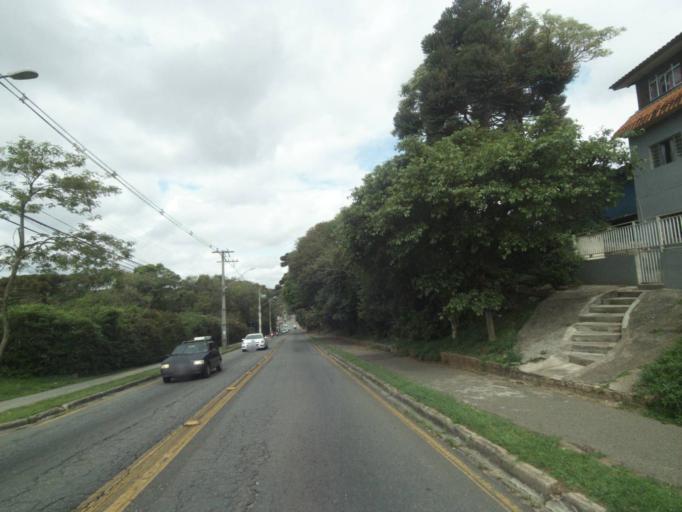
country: BR
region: Parana
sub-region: Curitiba
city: Curitiba
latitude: -25.3858
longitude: -49.2785
